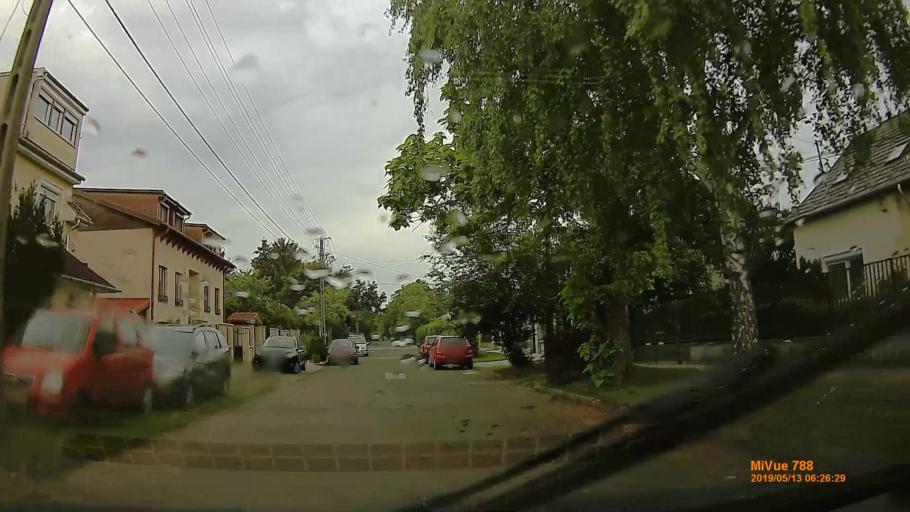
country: HU
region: Budapest
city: Budapest XXI. keruelet
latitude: 47.4245
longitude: 19.0821
